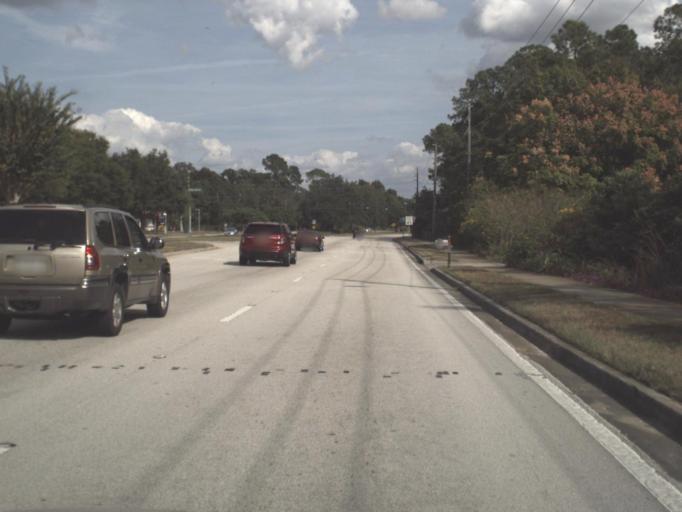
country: US
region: Florida
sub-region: Seminole County
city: Lake Mary
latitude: 28.7567
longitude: -81.2954
